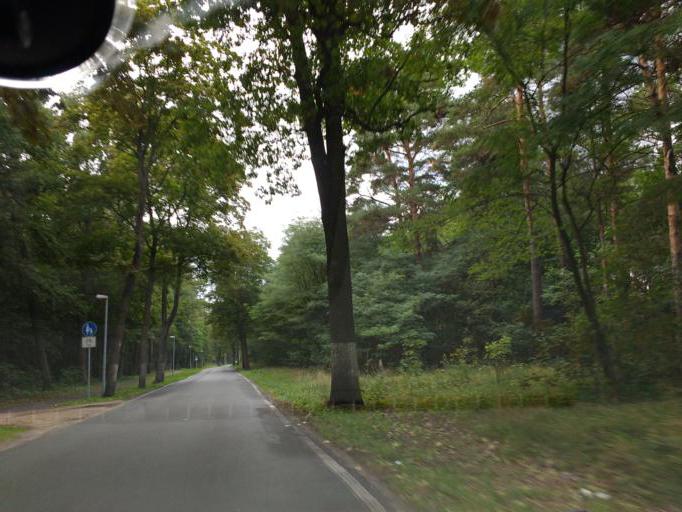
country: DE
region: Brandenburg
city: Bad Saarow
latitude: 52.2739
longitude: 14.0647
